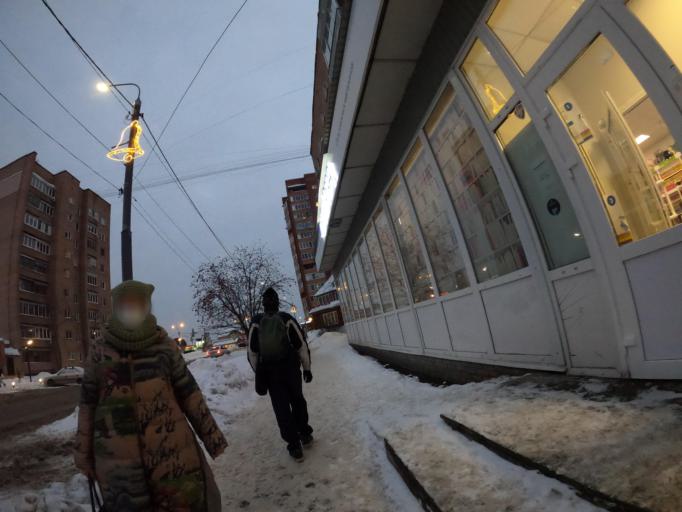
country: RU
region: Moskovskaya
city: Pavlovskiy Posad
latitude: 55.7782
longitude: 38.6714
